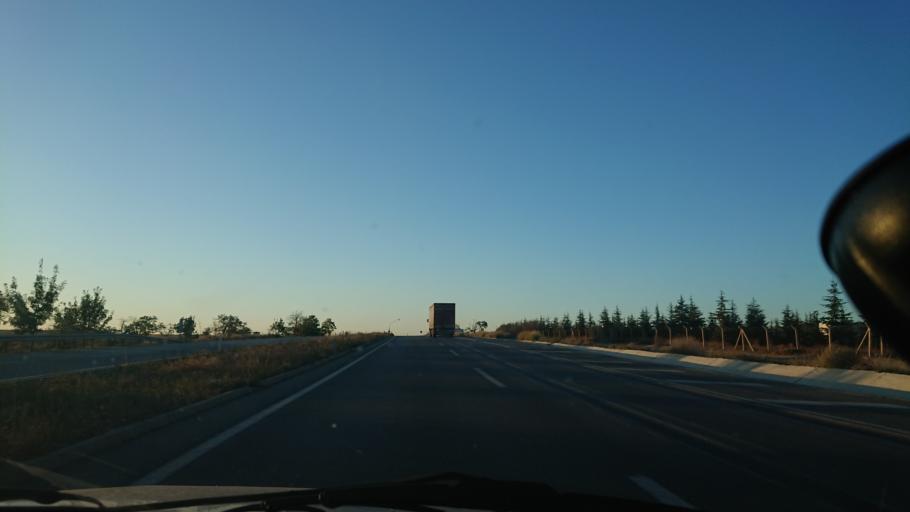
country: TR
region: Eskisehir
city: Mahmudiye
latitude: 39.4838
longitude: 30.9864
